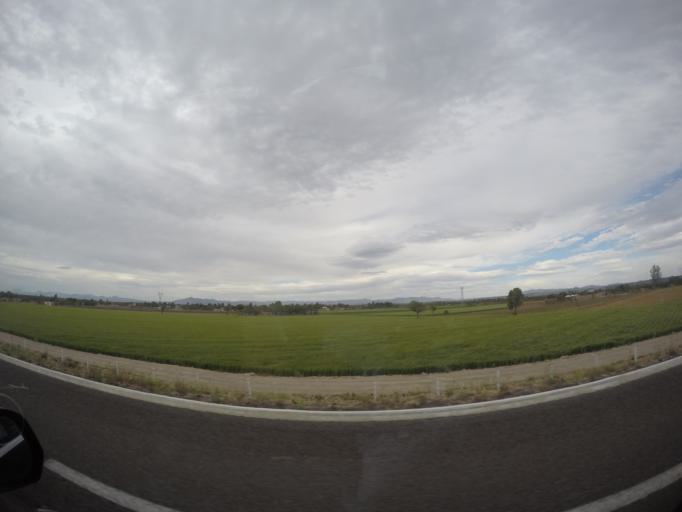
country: MX
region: Guanajuato
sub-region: Irapuato
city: Serrano
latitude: 20.8026
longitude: -101.4310
